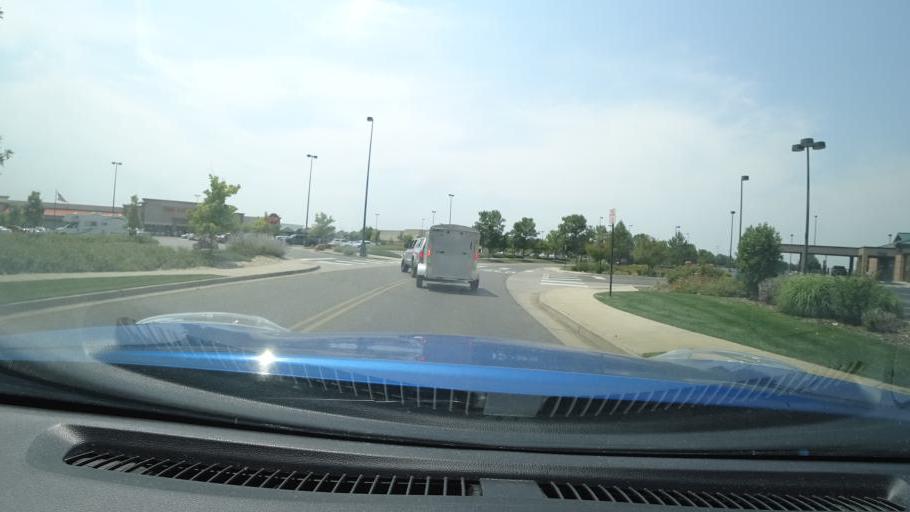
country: US
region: Colorado
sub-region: Adams County
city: Aurora
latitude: 39.7637
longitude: -104.7766
